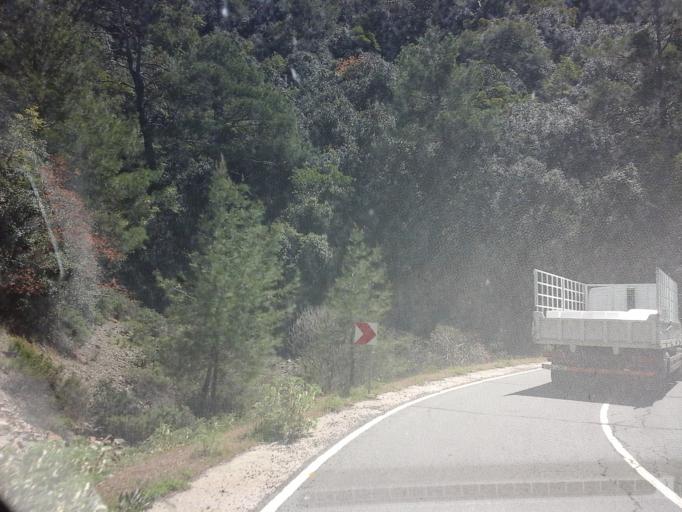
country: CY
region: Lefkosia
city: Kakopetria
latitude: 34.9938
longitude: 32.7928
